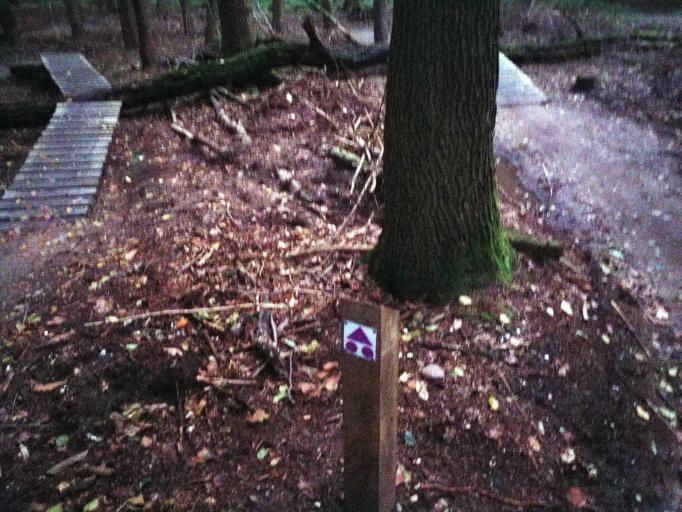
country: NL
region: Gelderland
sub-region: Gemeente Renkum
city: Doorwerth
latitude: 51.9835
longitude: 5.8169
